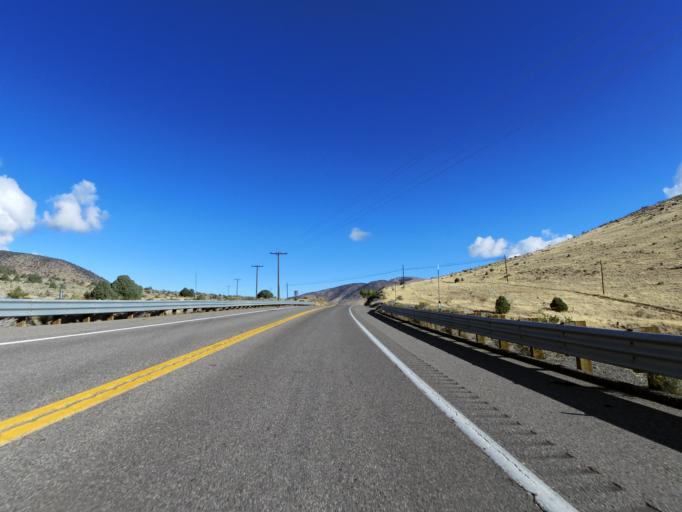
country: US
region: Nevada
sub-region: Lyon County
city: Smith Valley
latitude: 38.7091
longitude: -119.5530
